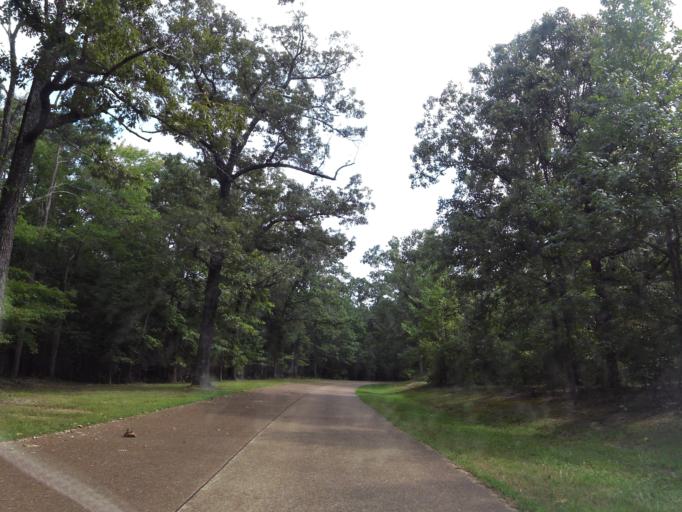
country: US
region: Tennessee
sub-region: Hardin County
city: Crump
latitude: 35.1270
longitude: -88.3566
